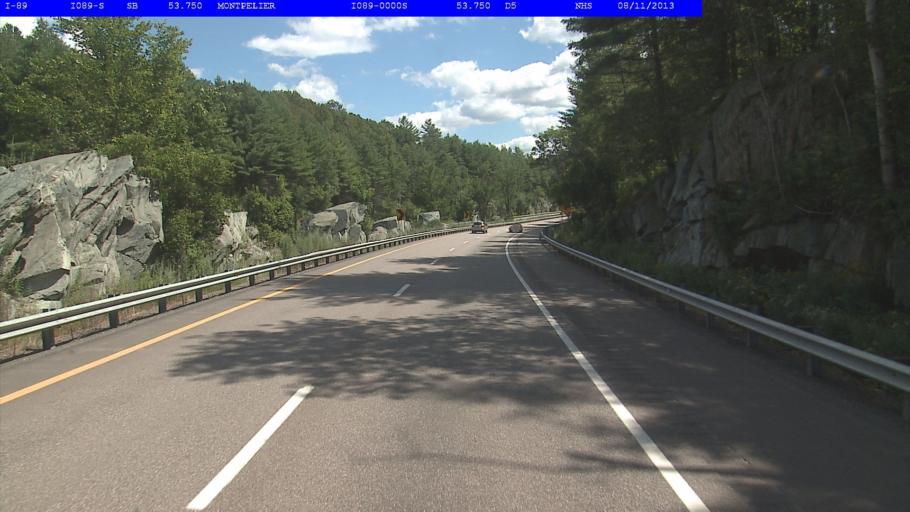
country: US
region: Vermont
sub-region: Washington County
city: Montpelier
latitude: 44.2602
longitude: -72.6038
